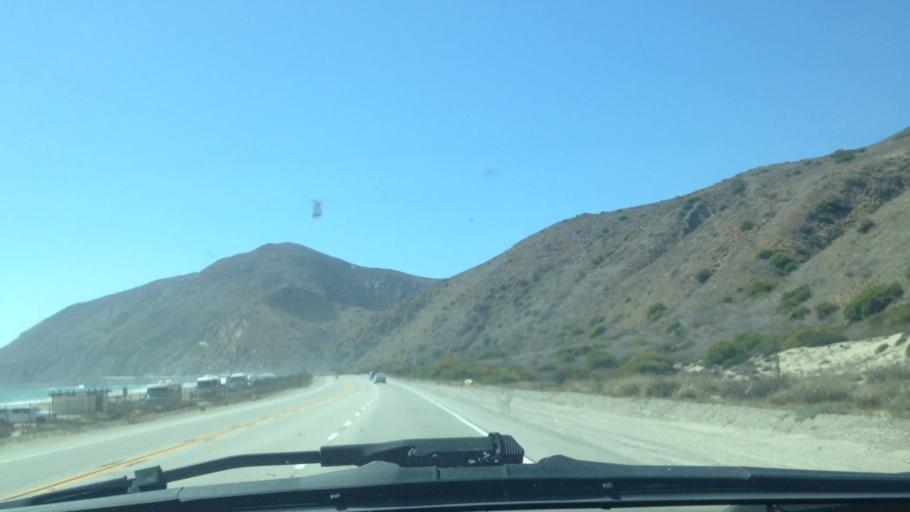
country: US
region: California
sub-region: Ventura County
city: Casa Conejo
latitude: 34.0786
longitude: -119.0262
